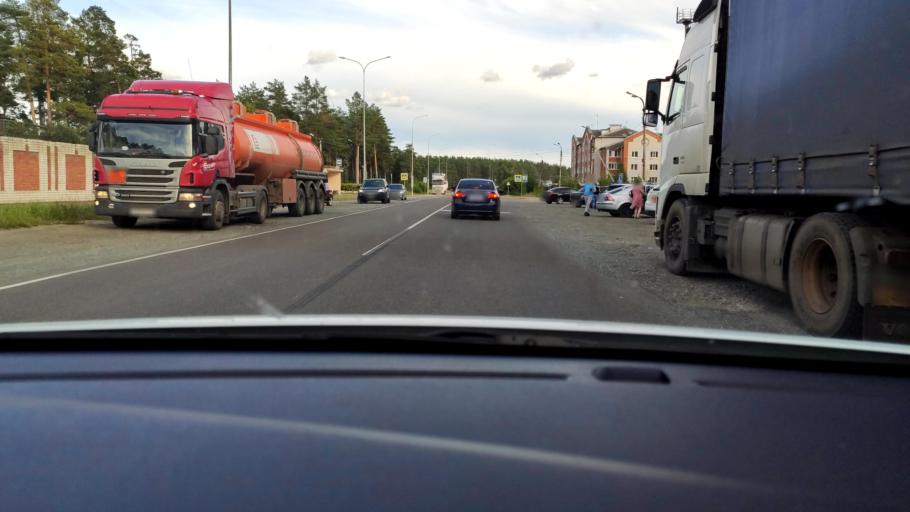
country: RU
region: Mariy-El
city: Suslonger
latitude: 56.3801
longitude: 48.2011
